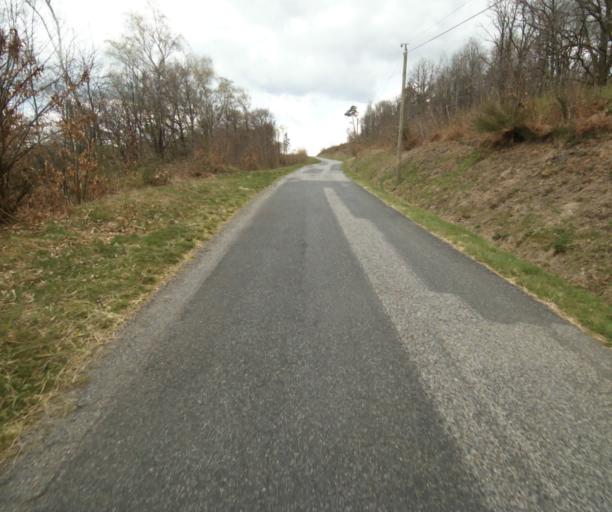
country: FR
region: Limousin
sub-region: Departement de la Correze
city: Correze
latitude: 45.2654
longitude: 1.9017
